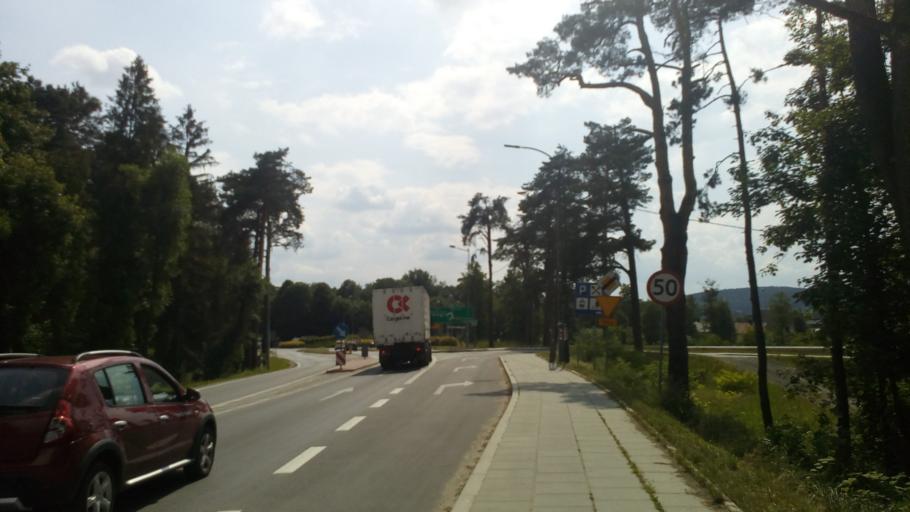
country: PL
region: Lesser Poland Voivodeship
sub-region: Powiat nowosadecki
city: Stary Sacz
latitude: 49.5685
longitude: 20.6581
